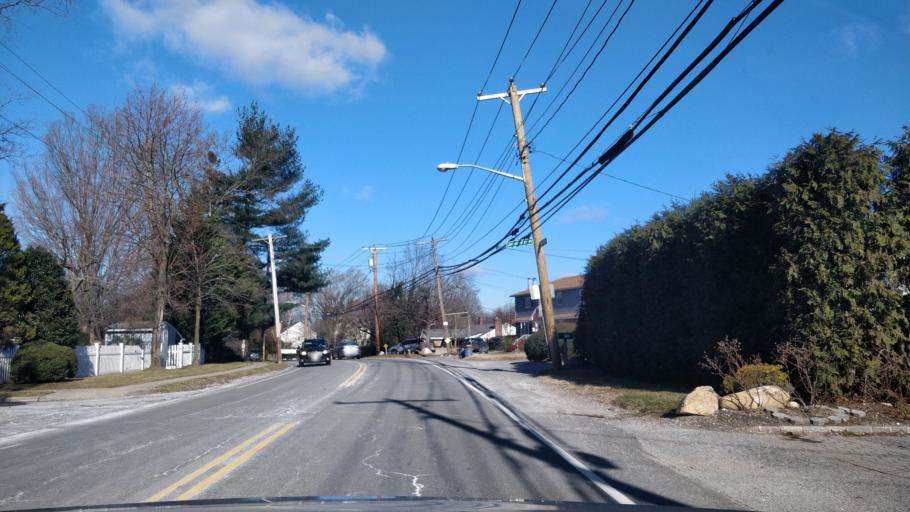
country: US
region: New York
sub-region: Nassau County
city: Glen Head
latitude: 40.8234
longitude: -73.6266
